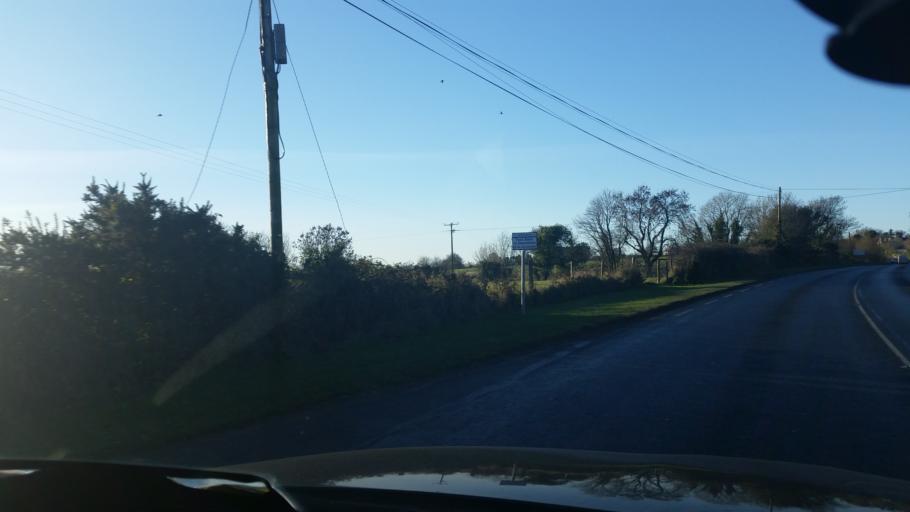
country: IE
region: Leinster
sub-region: Loch Garman
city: Ballinroad
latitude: 52.5637
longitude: -6.3301
